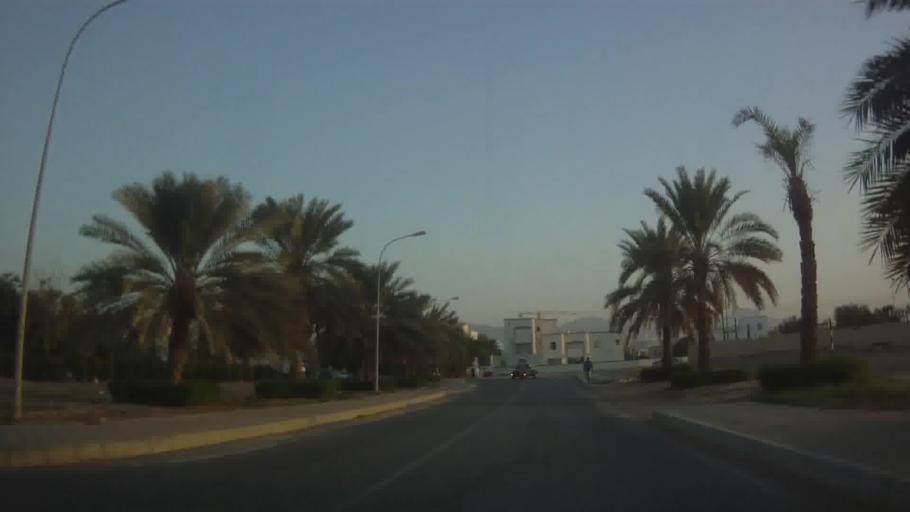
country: OM
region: Muhafazat Masqat
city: Bawshar
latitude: 23.5993
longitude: 58.4032
